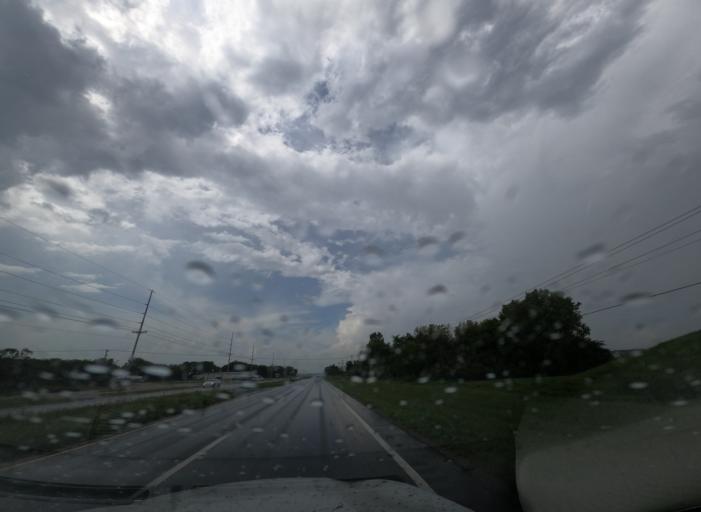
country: US
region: Alabama
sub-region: Morgan County
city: Trinity
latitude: 34.6258
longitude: -87.0862
